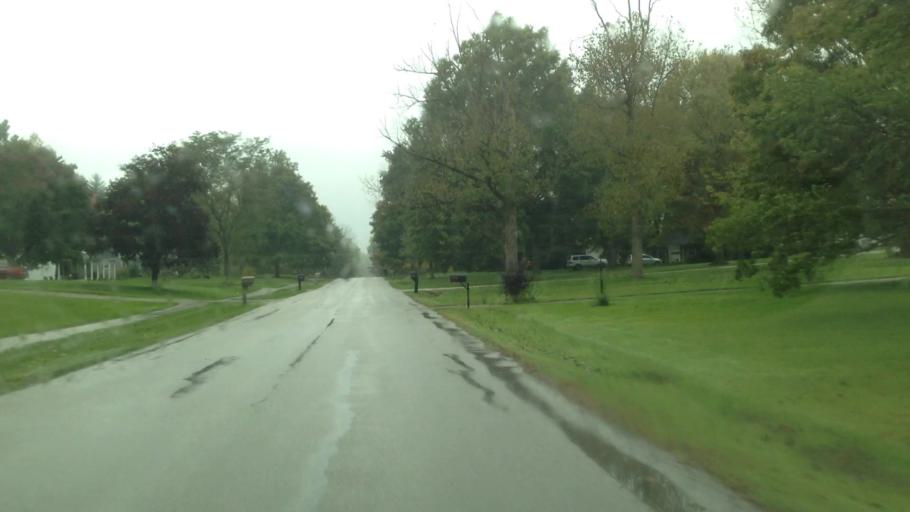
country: US
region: Ohio
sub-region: Summit County
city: Hudson
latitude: 41.2552
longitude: -81.4217
